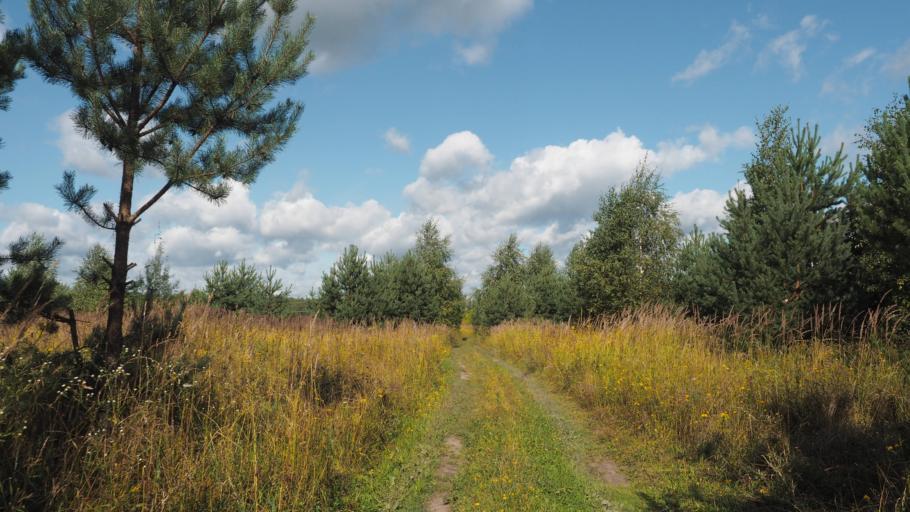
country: RU
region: Moskovskaya
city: Ramenskoye
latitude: 55.5977
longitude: 38.2843
